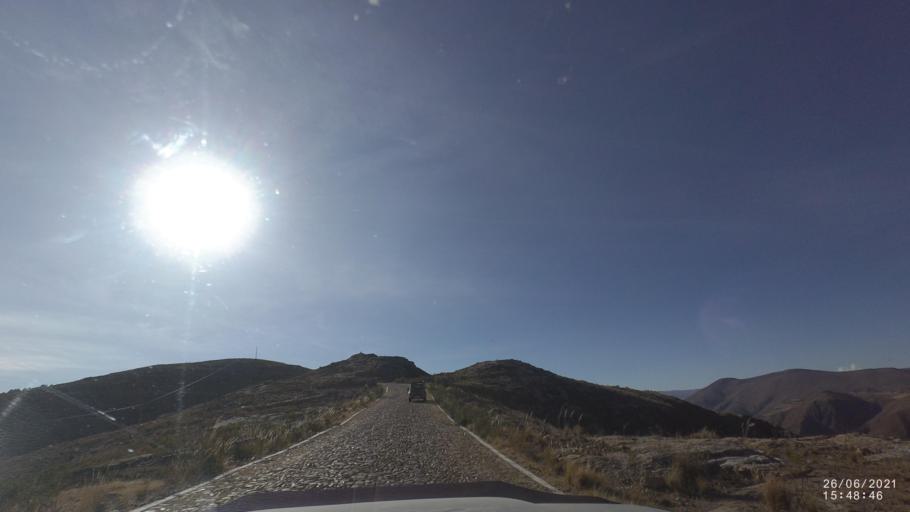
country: BO
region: Cochabamba
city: Arani
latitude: -17.8601
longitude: -65.6956
